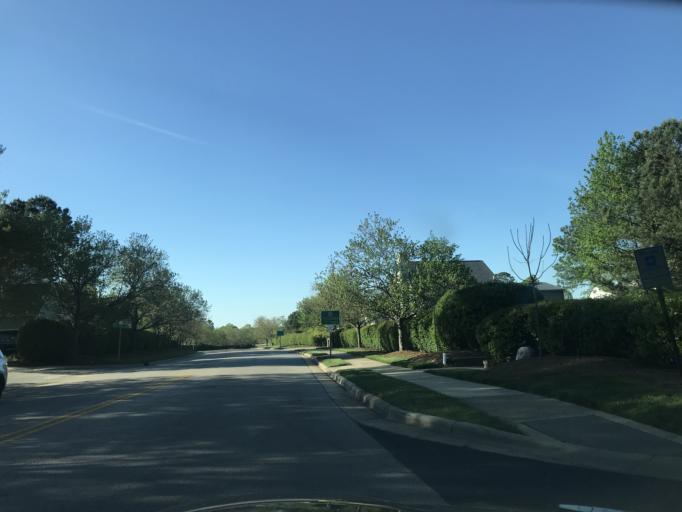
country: US
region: North Carolina
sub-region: Wake County
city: Knightdale
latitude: 35.8334
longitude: -78.5604
